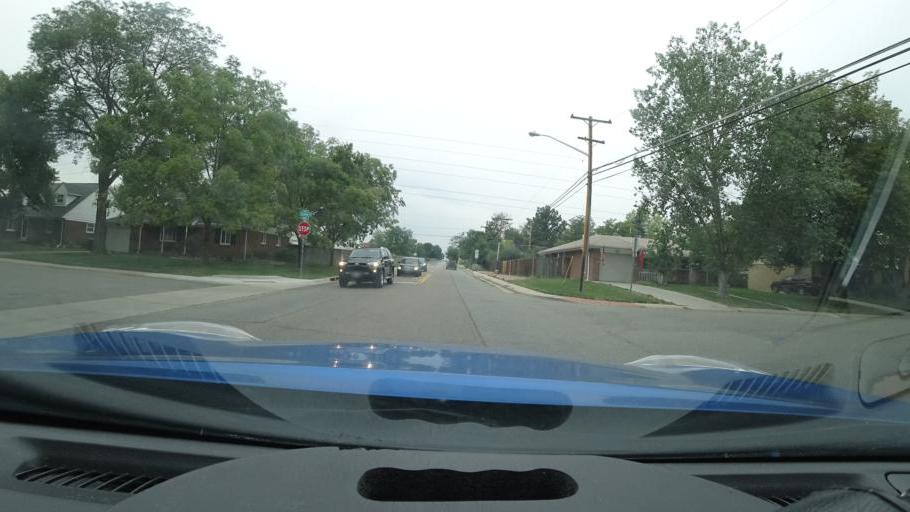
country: US
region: Colorado
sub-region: Arapahoe County
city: Glendale
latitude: 39.6821
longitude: -104.9169
